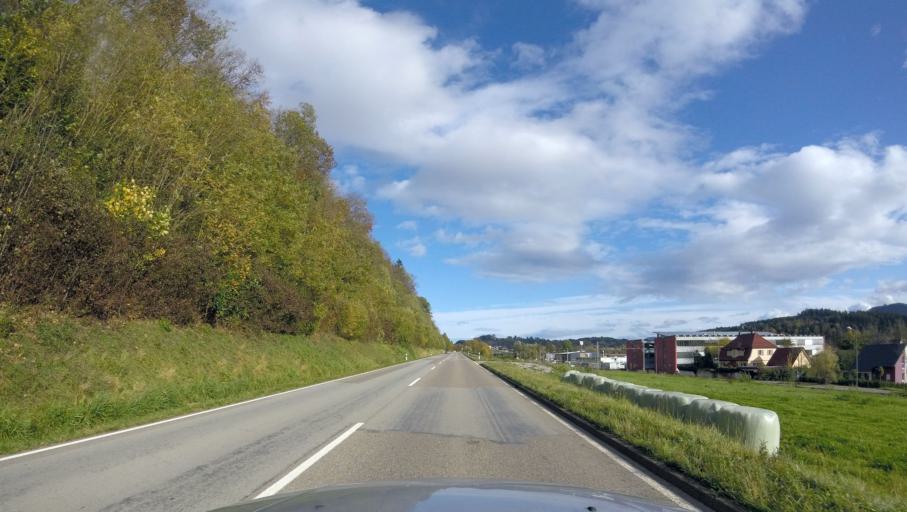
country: DE
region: Baden-Wuerttemberg
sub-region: Regierungsbezirk Stuttgart
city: Schwabisch Gmund
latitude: 48.7894
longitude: 9.7548
